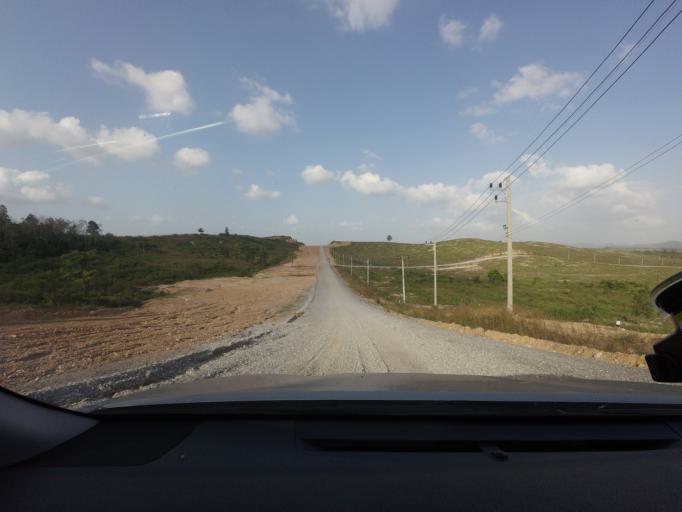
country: TH
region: Pattani
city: Mae Lan
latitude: 6.6047
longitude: 101.2500
